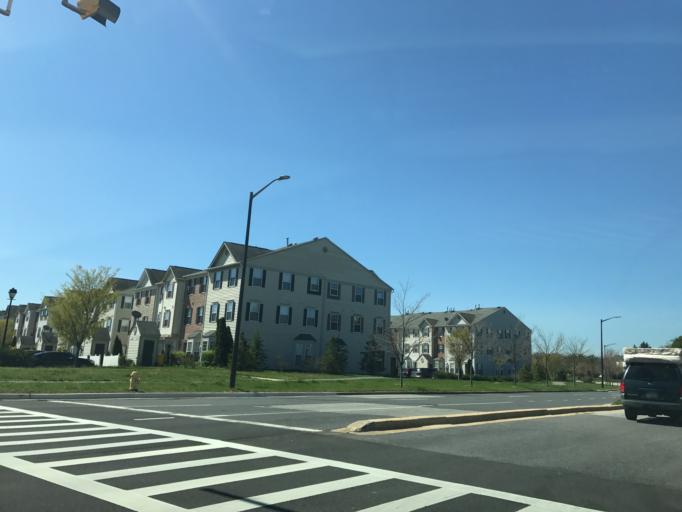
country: US
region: Maryland
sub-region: Anne Arundel County
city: Odenton
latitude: 39.1033
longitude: -76.7079
